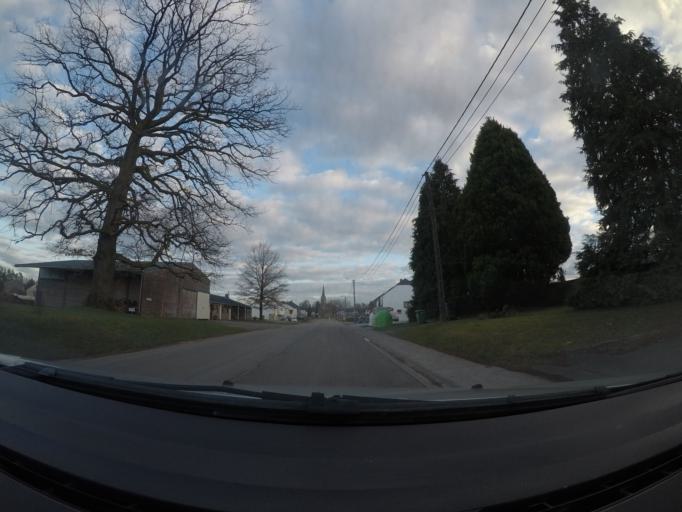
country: BE
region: Wallonia
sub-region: Province du Luxembourg
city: Etalle
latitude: 49.6617
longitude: 5.5718
